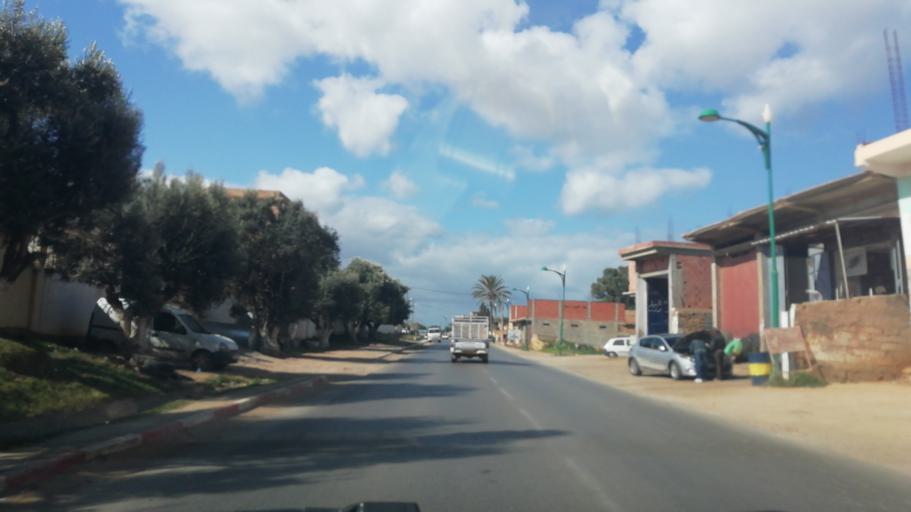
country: DZ
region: Relizane
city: Mazouna
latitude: 36.2631
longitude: 0.6174
